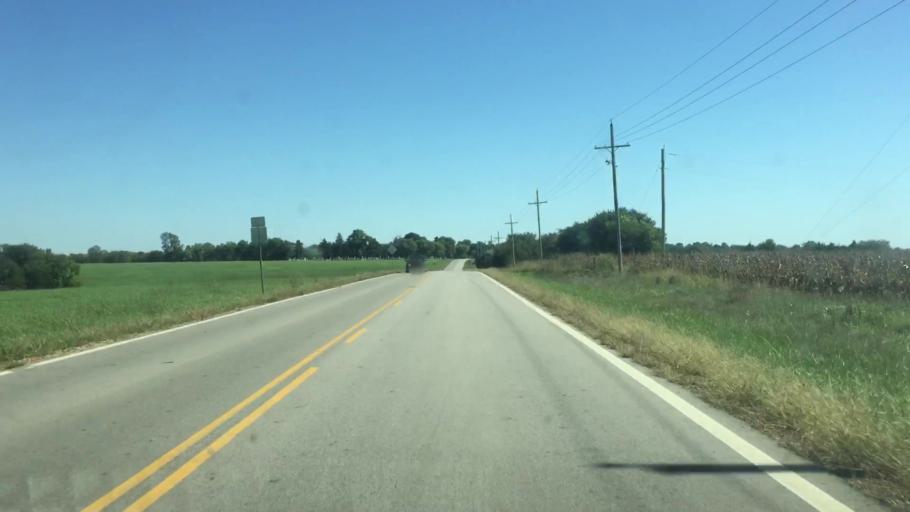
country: US
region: Kansas
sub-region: Jackson County
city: Holton
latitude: 39.6118
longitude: -95.7285
